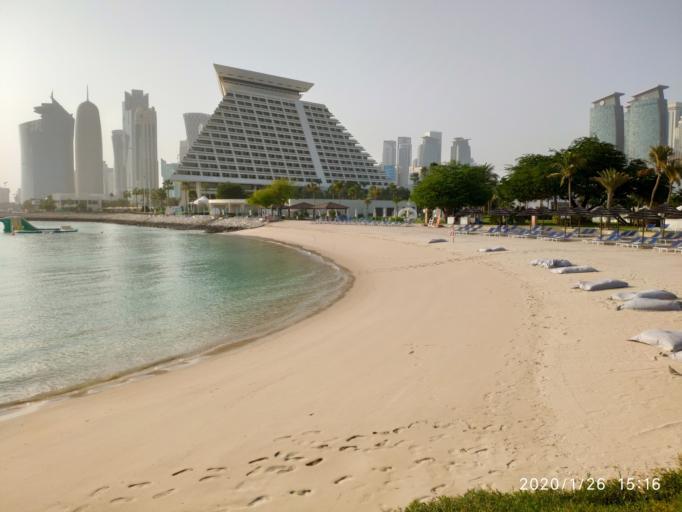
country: QA
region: Baladiyat ad Dawhah
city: Doha
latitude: 25.3175
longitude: 51.5391
